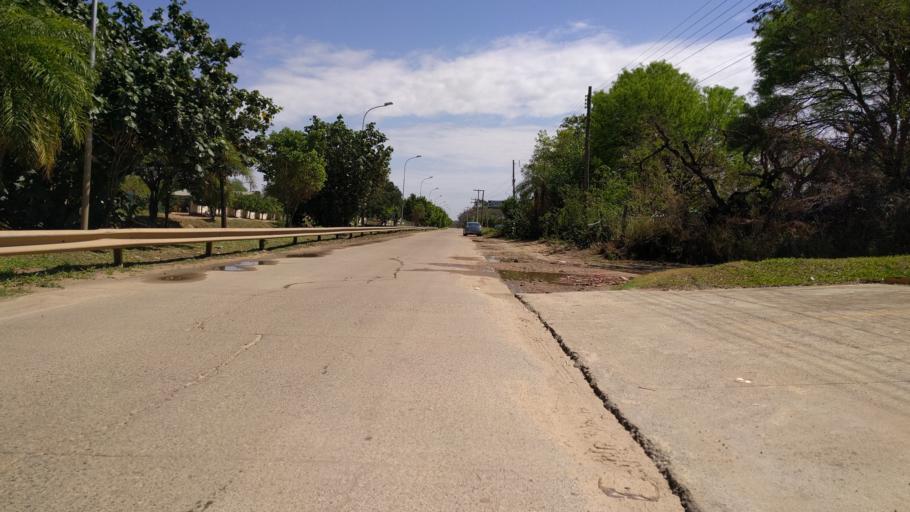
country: BO
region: Santa Cruz
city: Santa Cruz de la Sierra
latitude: -17.8155
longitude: -63.2275
